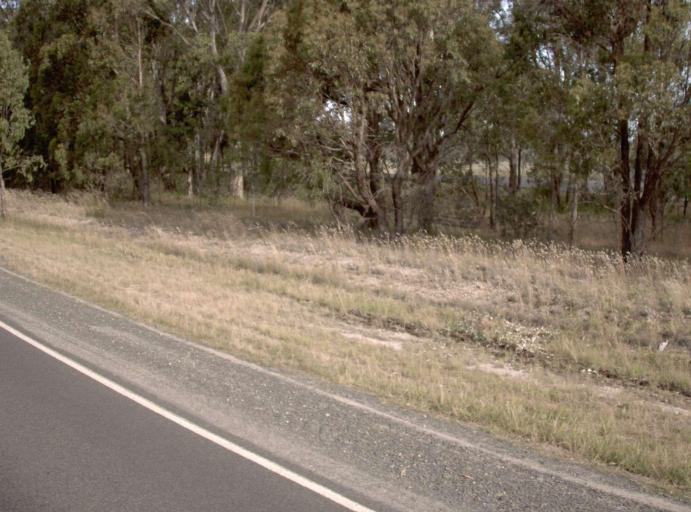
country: AU
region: Victoria
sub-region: Latrobe
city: Traralgon
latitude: -38.0598
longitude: 146.6306
